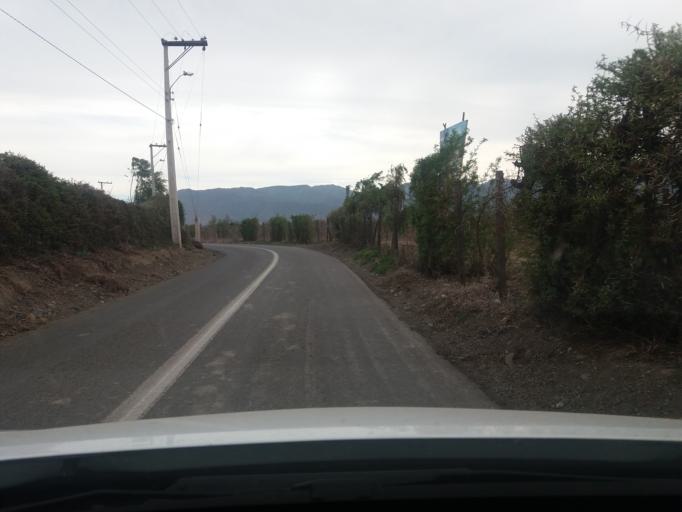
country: CL
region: Valparaiso
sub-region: Provincia de Los Andes
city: Los Andes
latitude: -32.8512
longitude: -70.6376
